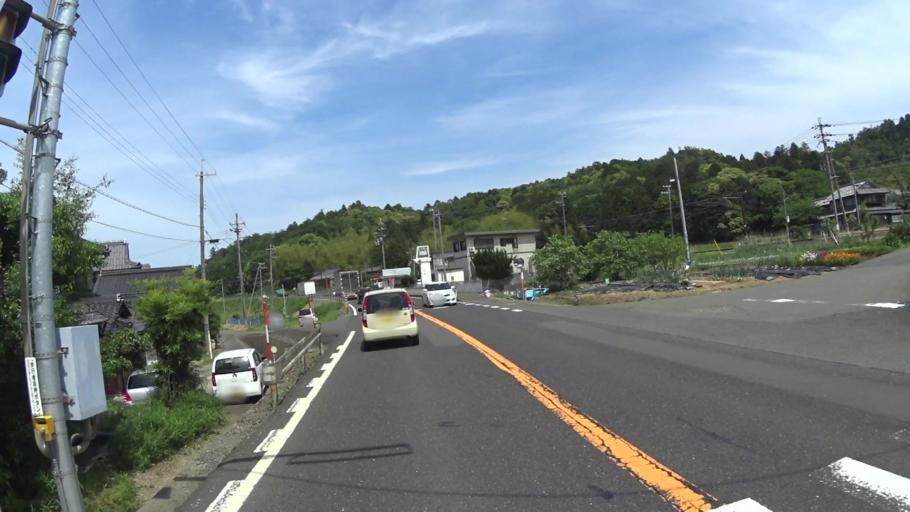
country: JP
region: Fukui
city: Obama
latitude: 35.4782
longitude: 135.6530
